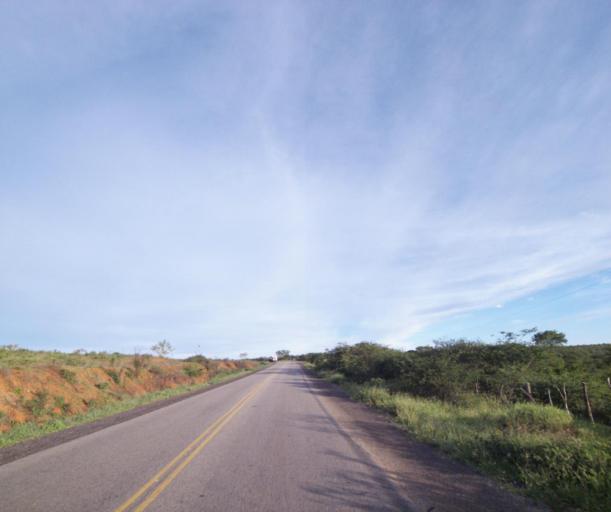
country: BR
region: Bahia
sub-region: Cacule
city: Cacule
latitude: -14.2100
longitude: -42.0990
